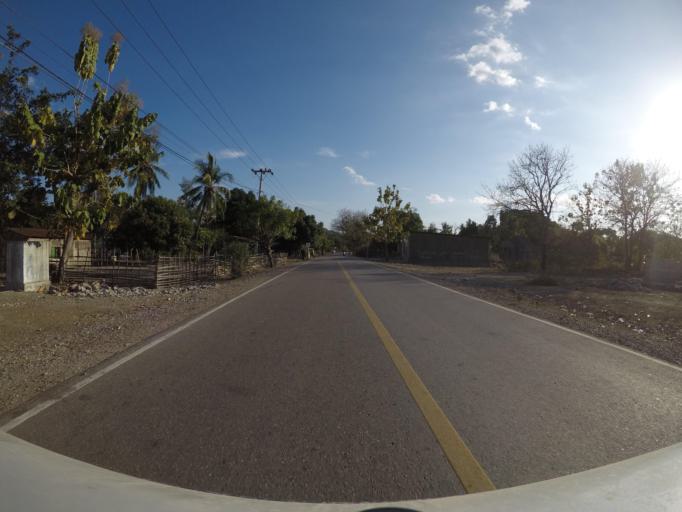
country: ID
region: East Nusa Tenggara
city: Atambua
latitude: -8.9425
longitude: 124.9783
